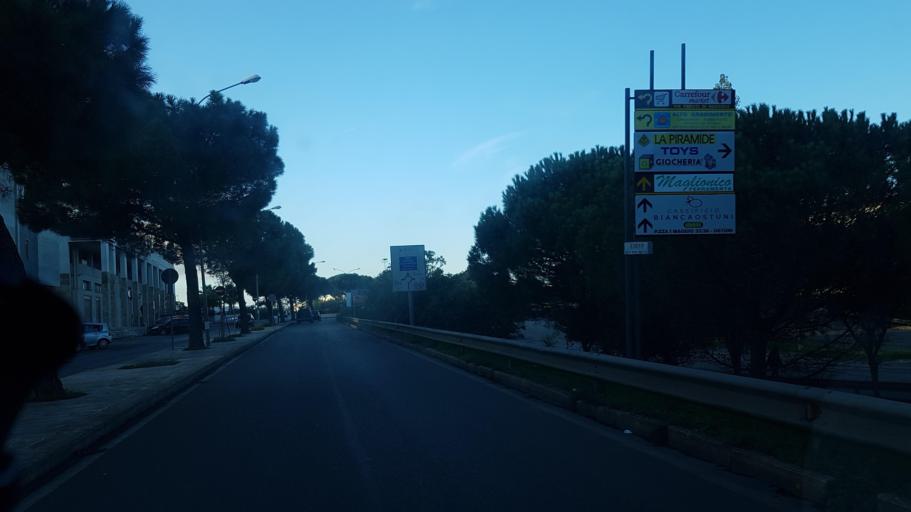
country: IT
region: Apulia
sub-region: Provincia di Brindisi
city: Ostuni
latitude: 40.7225
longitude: 17.5731
